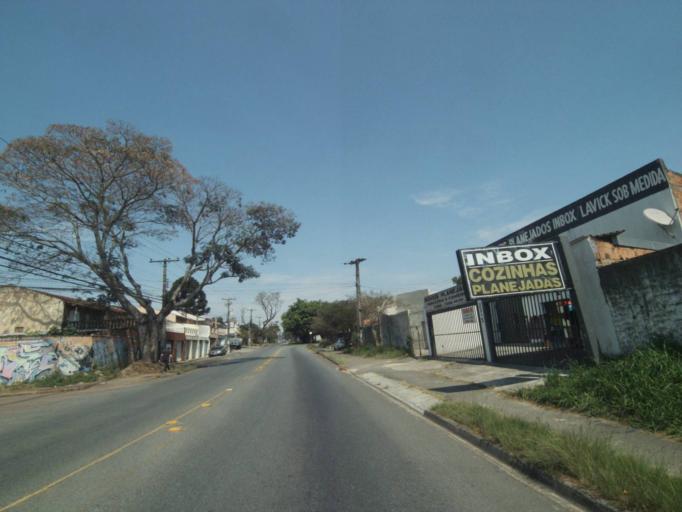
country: BR
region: Parana
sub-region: Curitiba
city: Curitiba
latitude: -25.4828
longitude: -49.3229
